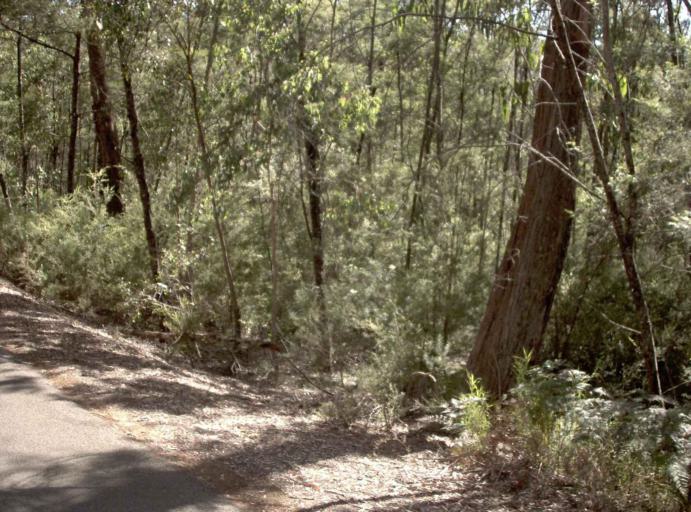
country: AU
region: Victoria
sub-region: East Gippsland
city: Lakes Entrance
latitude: -37.4710
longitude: 148.1237
